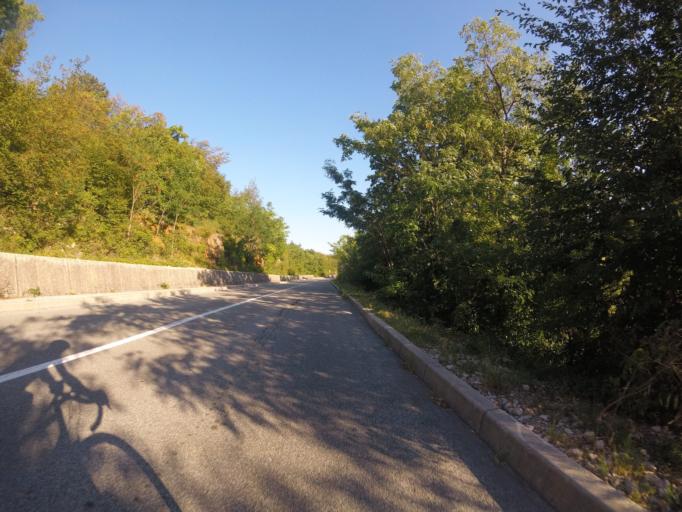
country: HR
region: Primorsko-Goranska
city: Selce
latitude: 45.1913
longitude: 14.7261
